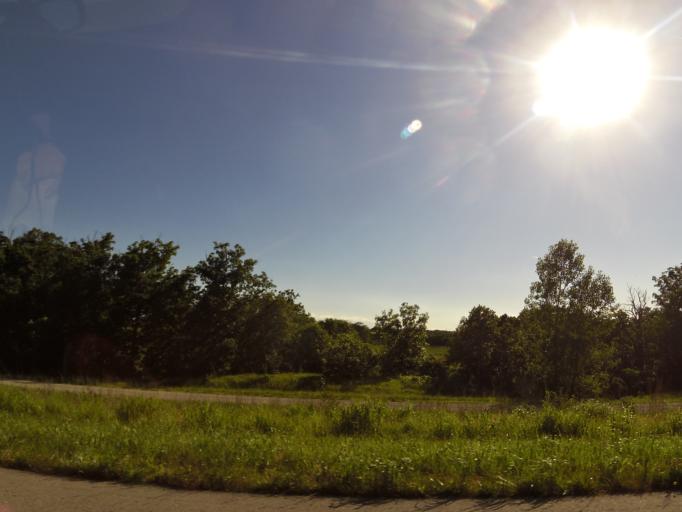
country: US
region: Missouri
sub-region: Pike County
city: Bowling Green
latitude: 39.4262
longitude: -91.2545
